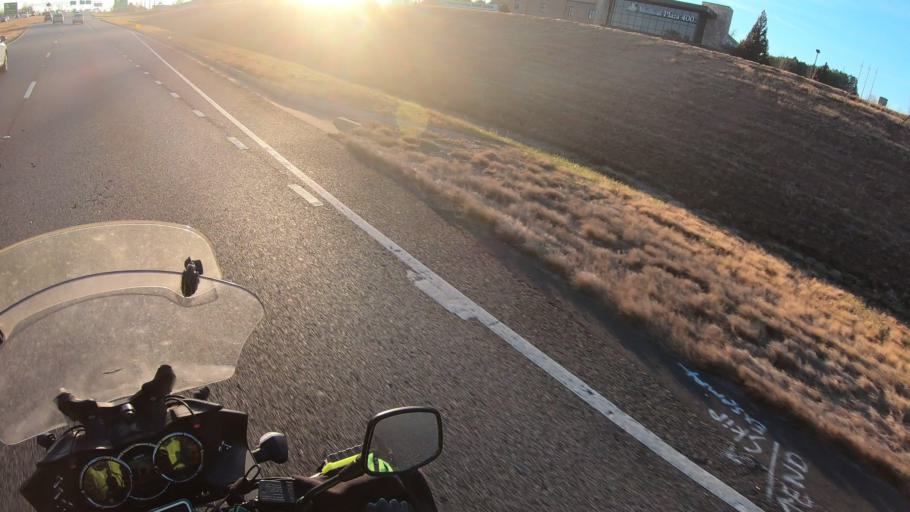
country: US
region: Georgia
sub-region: Dawson County
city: Dawsonville
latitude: 34.3677
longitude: -84.0316
